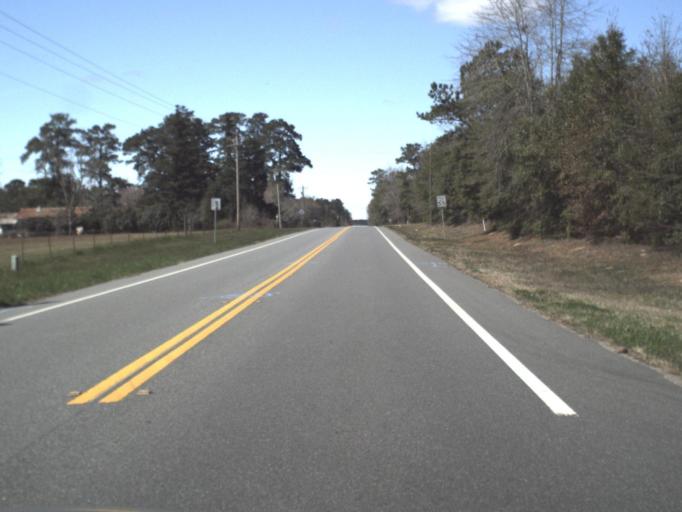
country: US
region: Florida
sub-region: Gadsden County
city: Gretna
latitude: 30.6627
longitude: -84.6951
